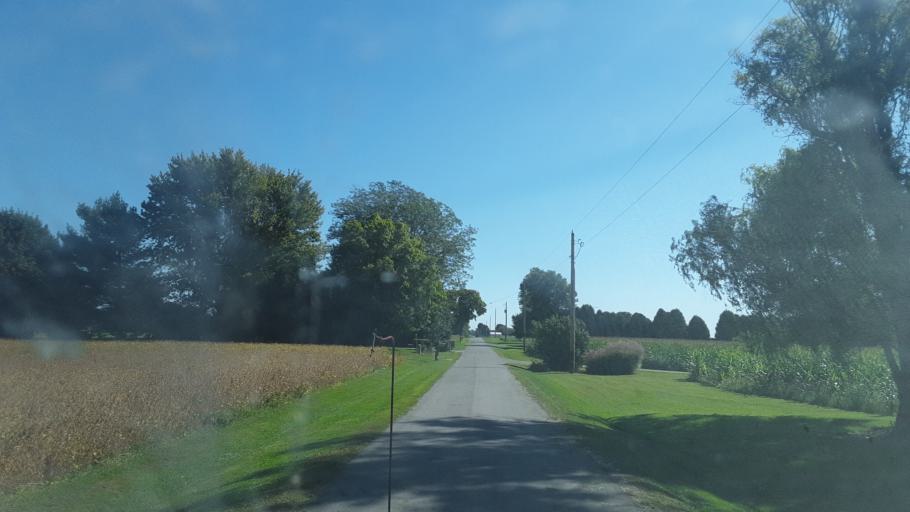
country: US
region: Ohio
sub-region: Wyandot County
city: Upper Sandusky
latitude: 40.9348
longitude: -83.2221
